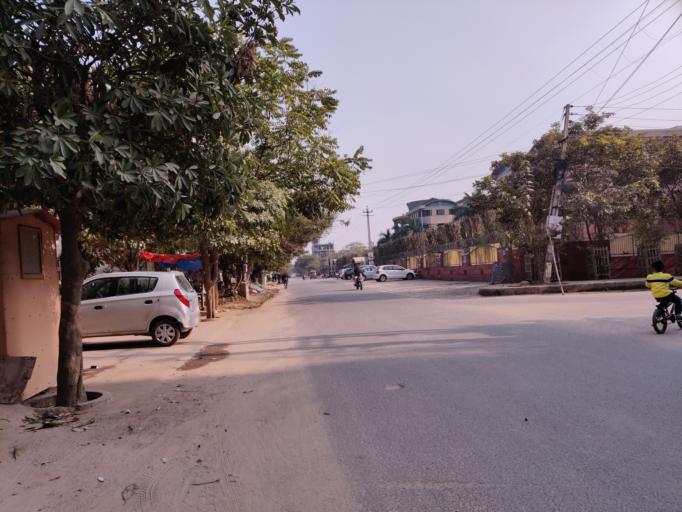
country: IN
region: Haryana
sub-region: Gurgaon
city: Gurgaon
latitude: 28.4428
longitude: 77.0646
